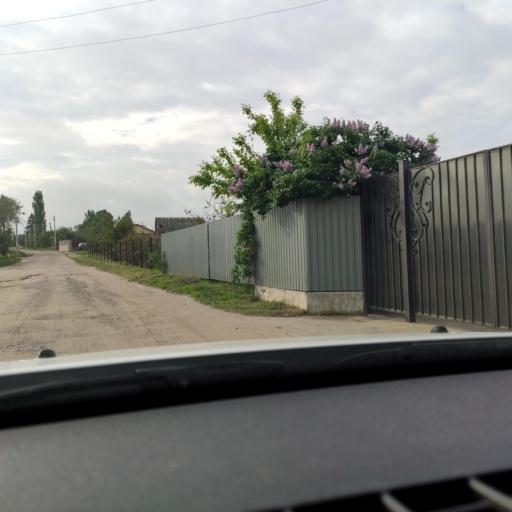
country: RU
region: Voronezj
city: Devitsa
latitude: 51.6420
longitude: 38.9540
